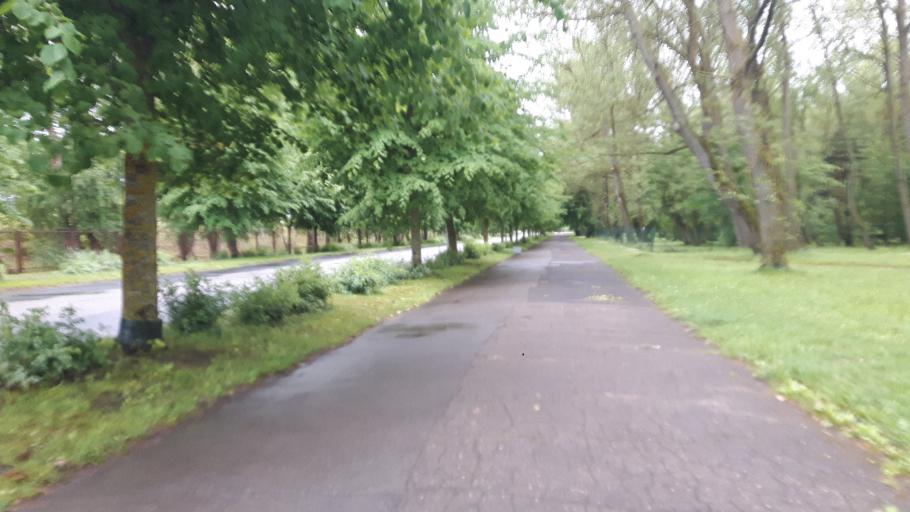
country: LV
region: Liepaja
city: Liepaja
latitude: 56.5135
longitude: 20.9912
